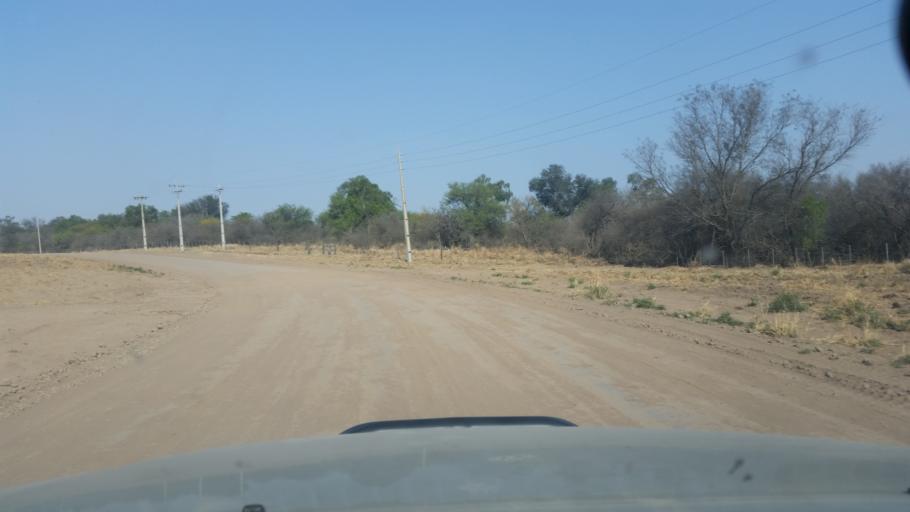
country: PY
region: Boqueron
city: Filadelfia
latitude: -22.0779
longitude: -60.6857
